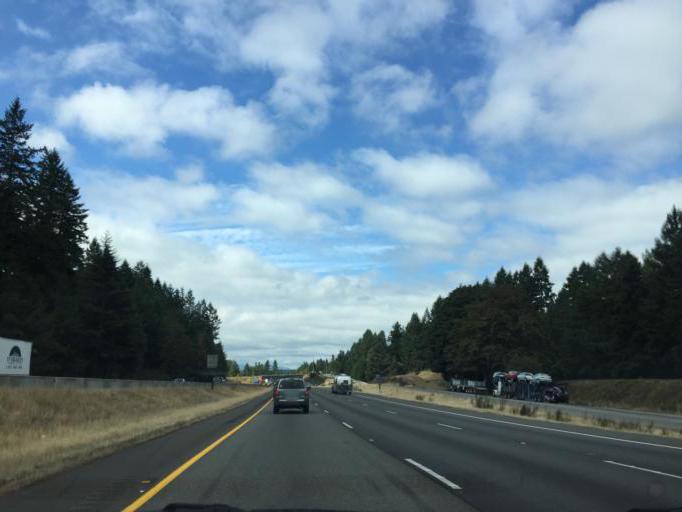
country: US
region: Washington
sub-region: Pierce County
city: DuPont
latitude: 47.0839
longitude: -122.6624
